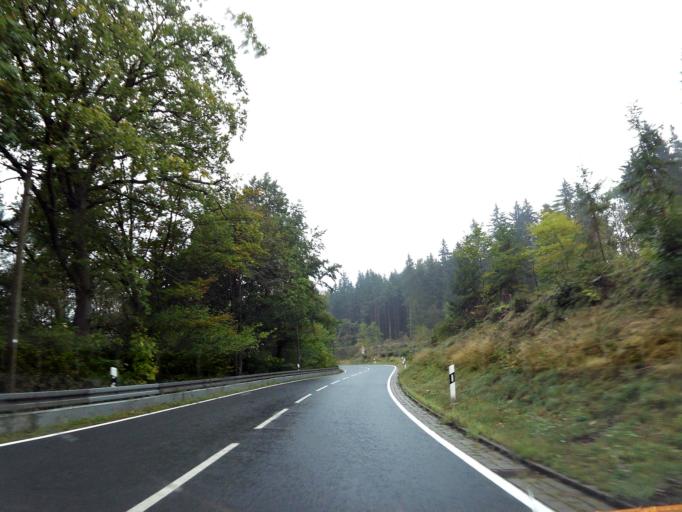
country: DE
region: Saxony-Anhalt
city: Stolberg
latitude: 51.6468
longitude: 10.9218
